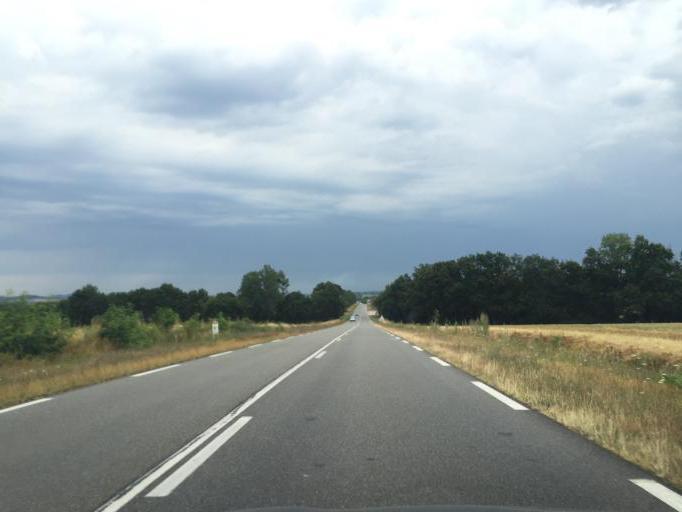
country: FR
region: Auvergne
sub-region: Departement de l'Allier
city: Lapalisse
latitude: 46.2479
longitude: 3.5971
